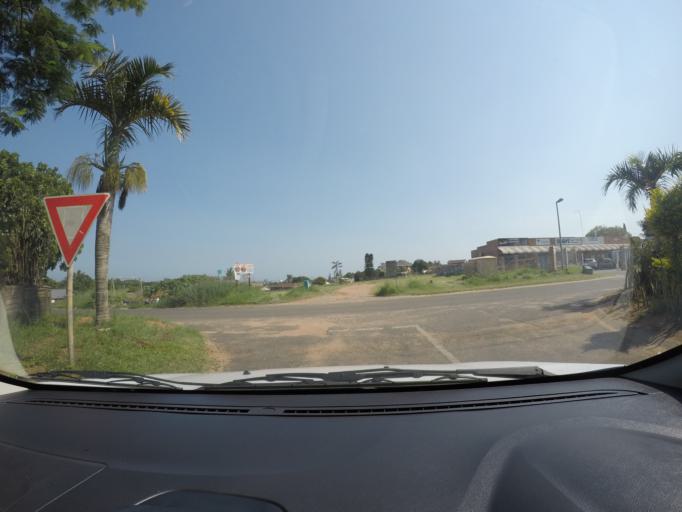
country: ZA
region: KwaZulu-Natal
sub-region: uThungulu District Municipality
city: Richards Bay
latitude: -28.7245
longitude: 32.0449
